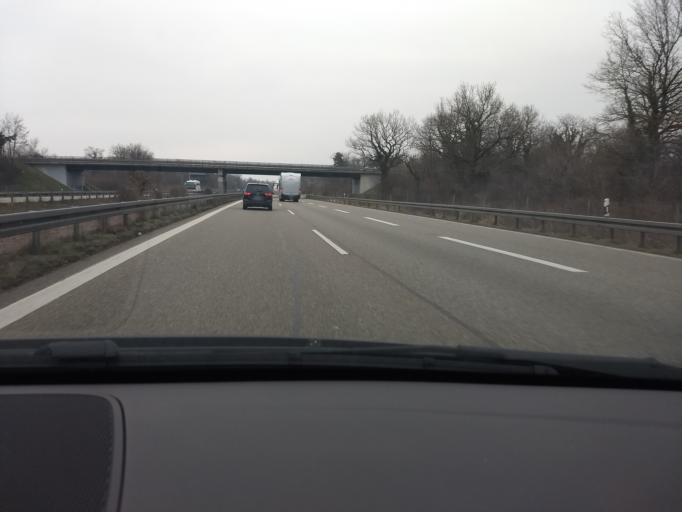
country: DE
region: Baden-Wuerttemberg
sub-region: Freiburg Region
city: Hartheim
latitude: 47.9073
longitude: 7.5889
